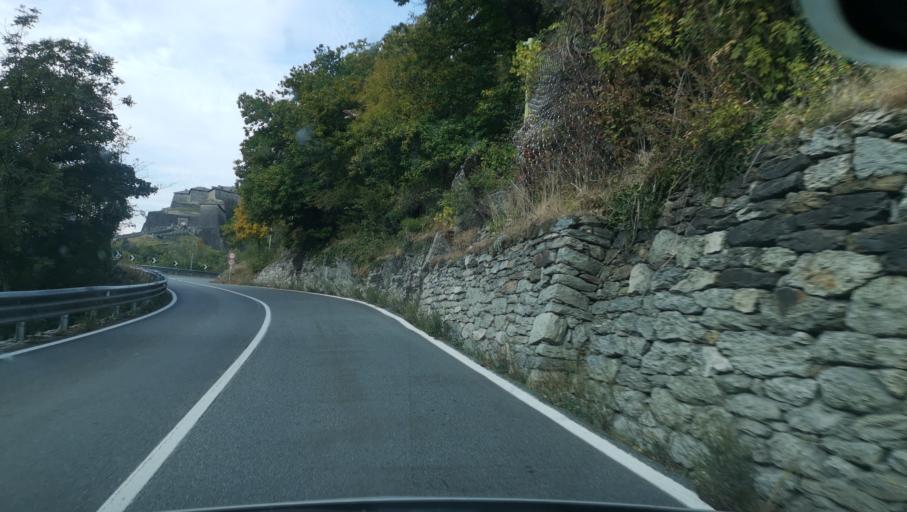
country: IT
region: Piedmont
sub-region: Provincia di Torino
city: Exilles
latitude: 45.1033
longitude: 6.9434
